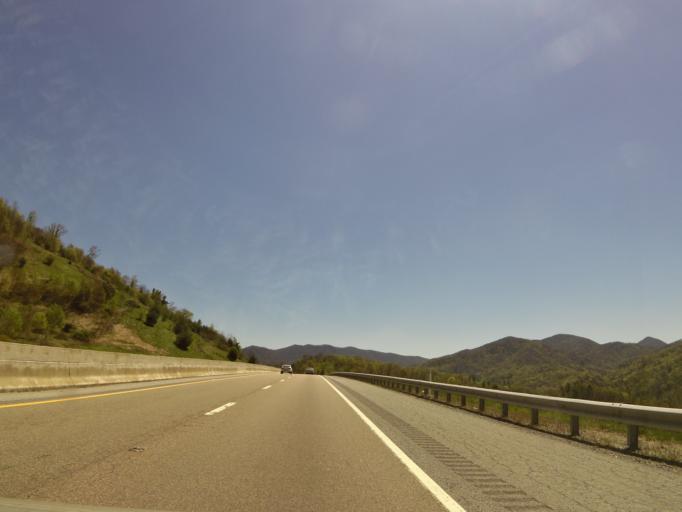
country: US
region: Tennessee
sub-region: Unicoi County
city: Banner Hill
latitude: 36.0233
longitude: -82.5454
